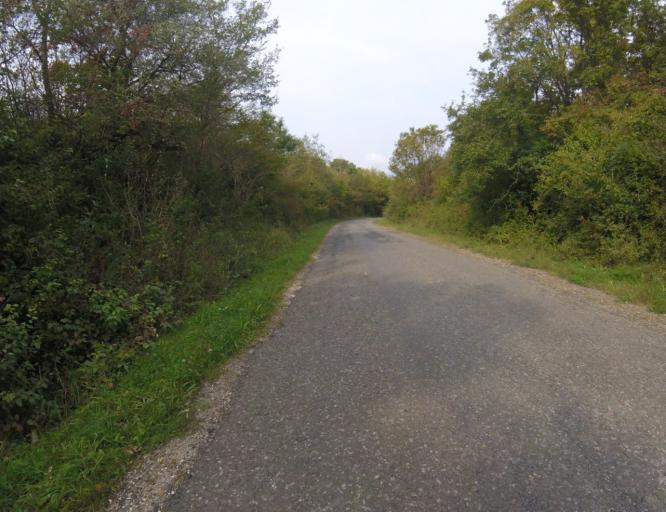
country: HU
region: Pest
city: Veroce
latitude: 47.8434
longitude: 19.0498
